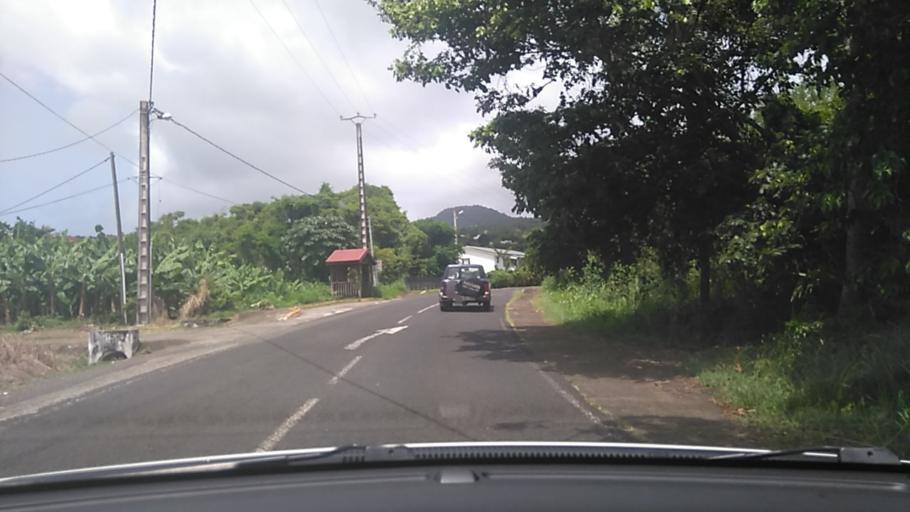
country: MQ
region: Martinique
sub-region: Martinique
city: Saint-Esprit
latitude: 14.5590
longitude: -60.9215
